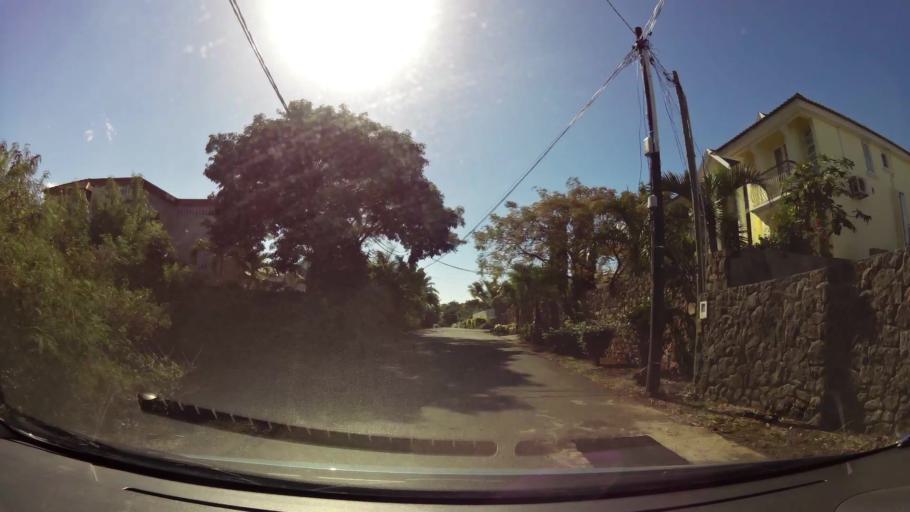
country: MU
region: Black River
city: Flic en Flac
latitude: -20.2633
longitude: 57.3777
